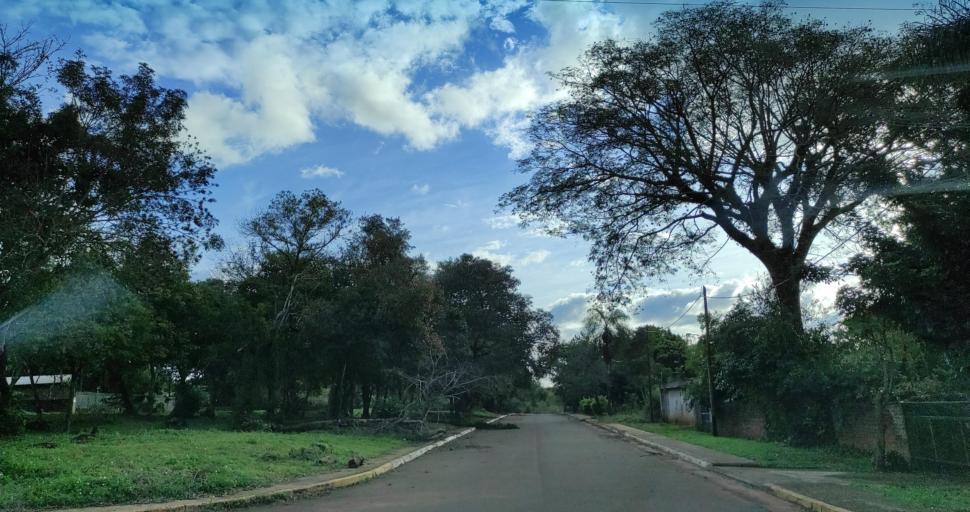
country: AR
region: Misiones
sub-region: Departamento de Candelaria
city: Candelaria
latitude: -27.4516
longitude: -55.7524
